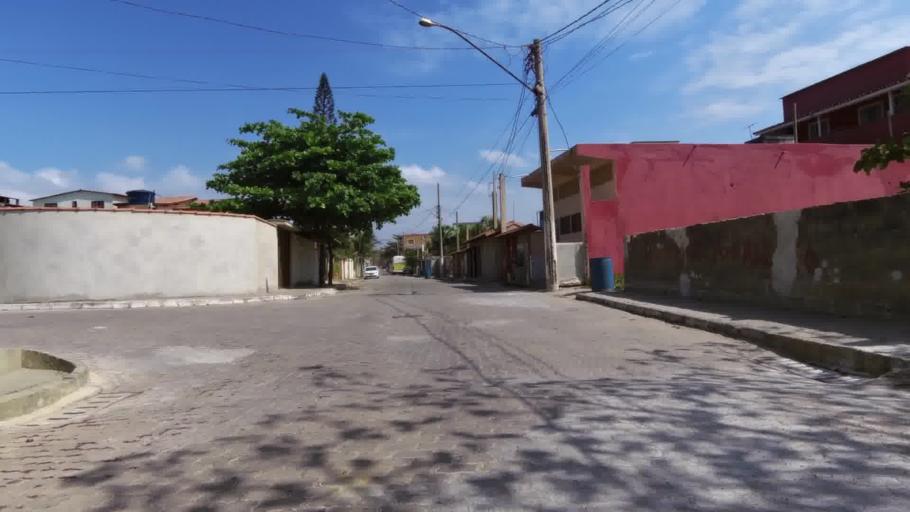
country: BR
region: Espirito Santo
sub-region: Marataizes
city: Marataizes
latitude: -21.0274
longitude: -40.8124
